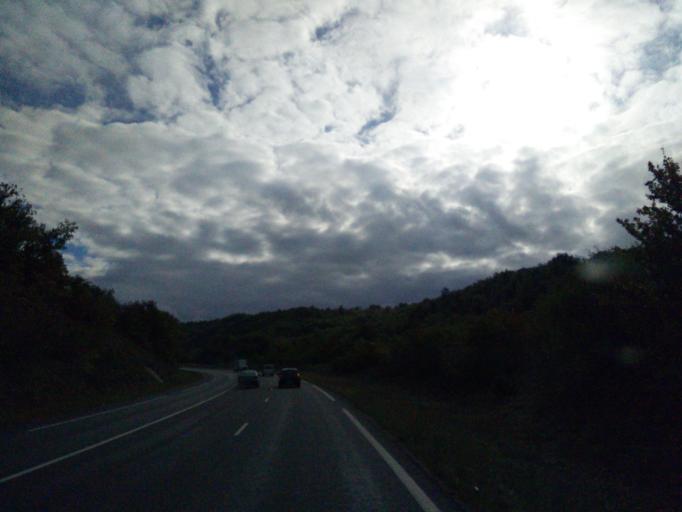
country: FR
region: Midi-Pyrenees
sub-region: Departement du Lot
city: Cahors
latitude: 44.4576
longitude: 1.4128
